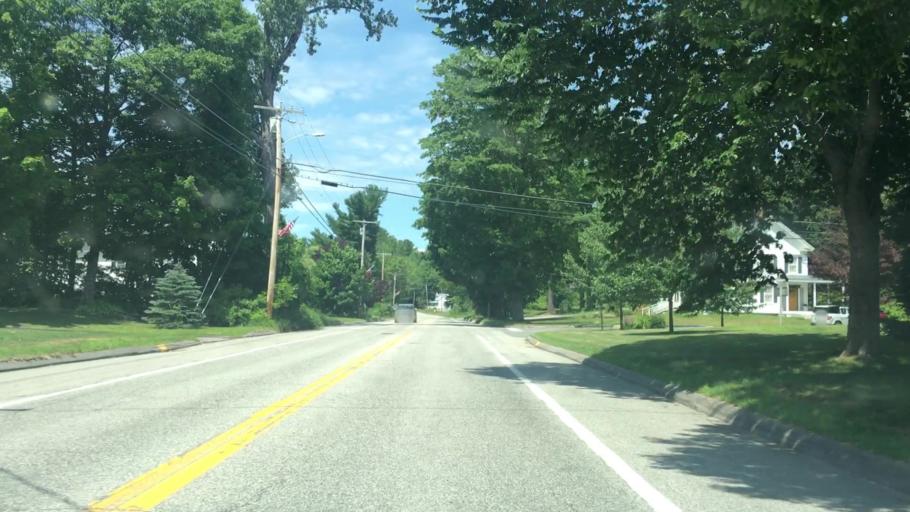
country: US
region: Maine
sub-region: Kennebec County
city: Wayne
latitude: 44.3509
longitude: -70.0709
